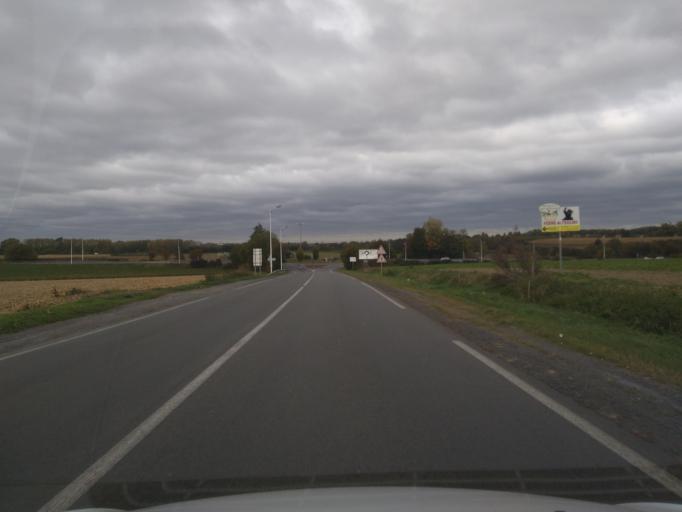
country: FR
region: Nord-Pas-de-Calais
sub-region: Departement du Nord
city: Marly
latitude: 50.3540
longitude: 3.5627
